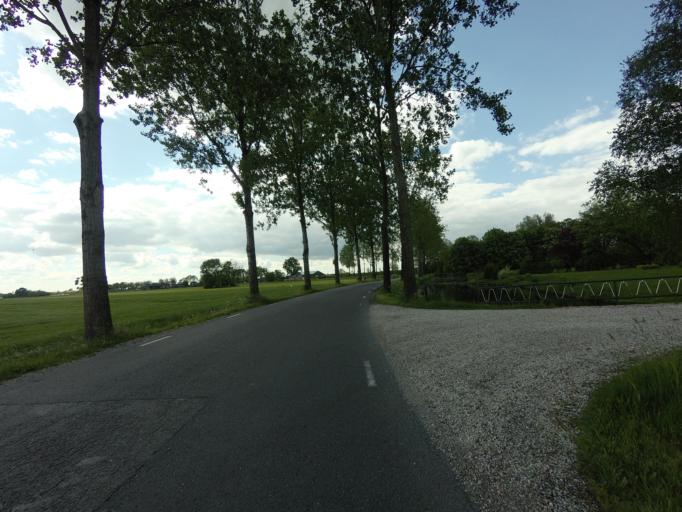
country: NL
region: South Holland
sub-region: Gemeente Leerdam
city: Leerdam
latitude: 51.9118
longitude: 5.0320
